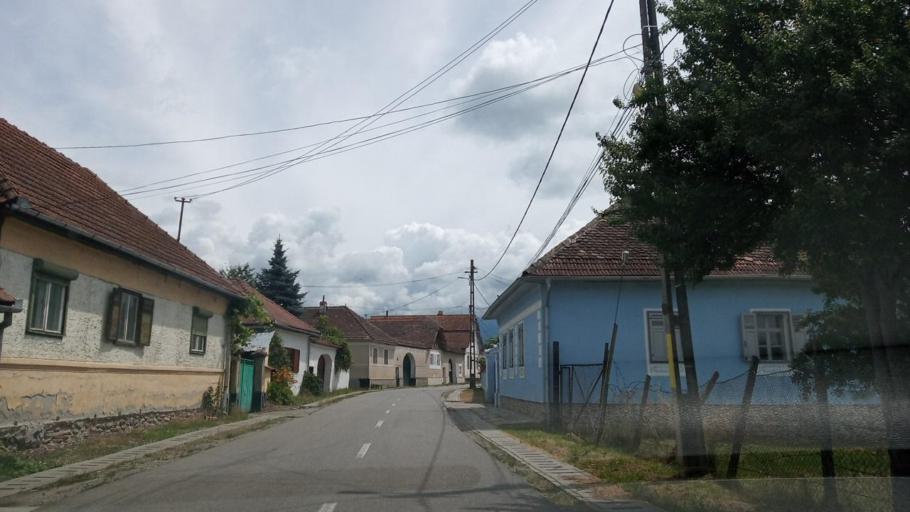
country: RO
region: Sibiu
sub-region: Comuna Porumbacu de Jos
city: Porumbacu de Jos
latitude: 45.7152
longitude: 24.4746
